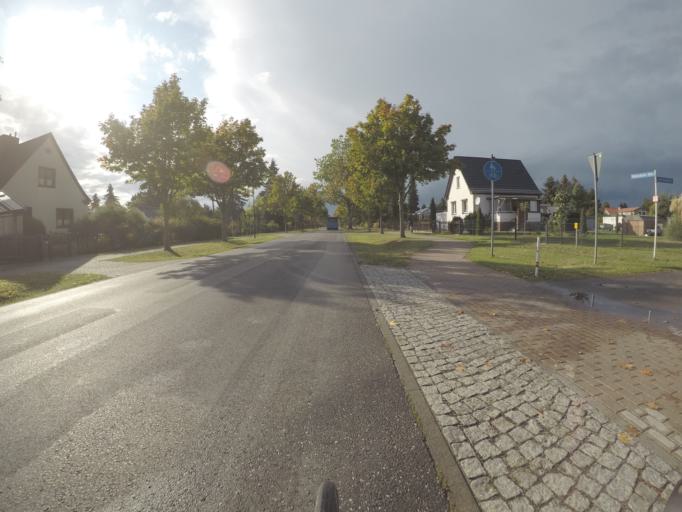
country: DE
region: Brandenburg
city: Petershagen
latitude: 52.5149
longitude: 13.7428
